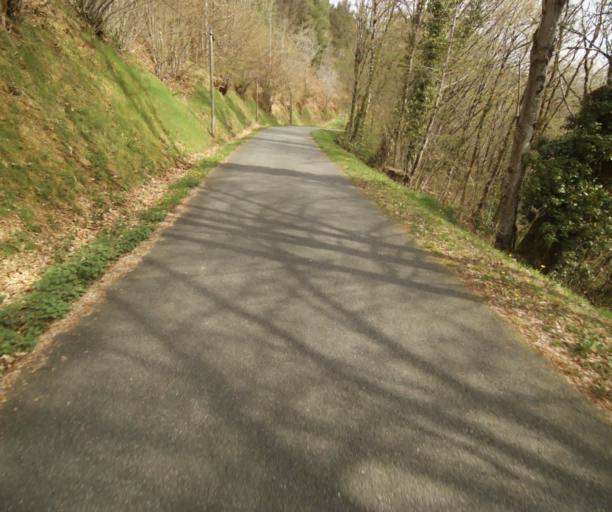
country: FR
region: Limousin
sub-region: Departement de la Correze
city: Naves
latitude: 45.3365
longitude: 1.8065
